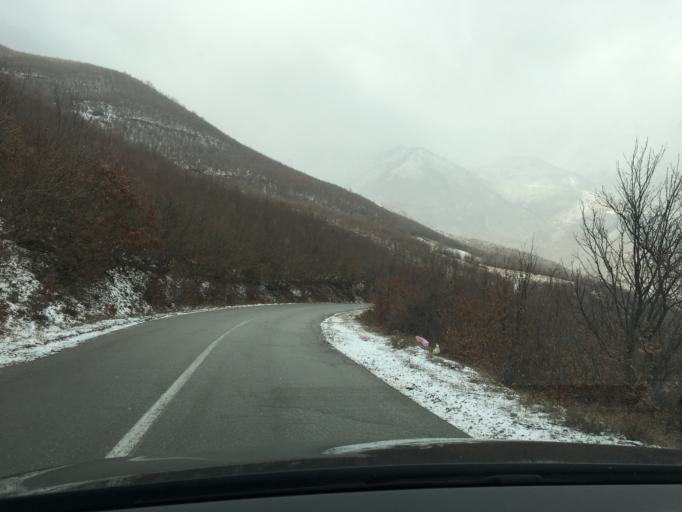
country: XK
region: Pec
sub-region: Komuna e Pejes
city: Dubova (Driloni)
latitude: 42.7508
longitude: 20.3037
